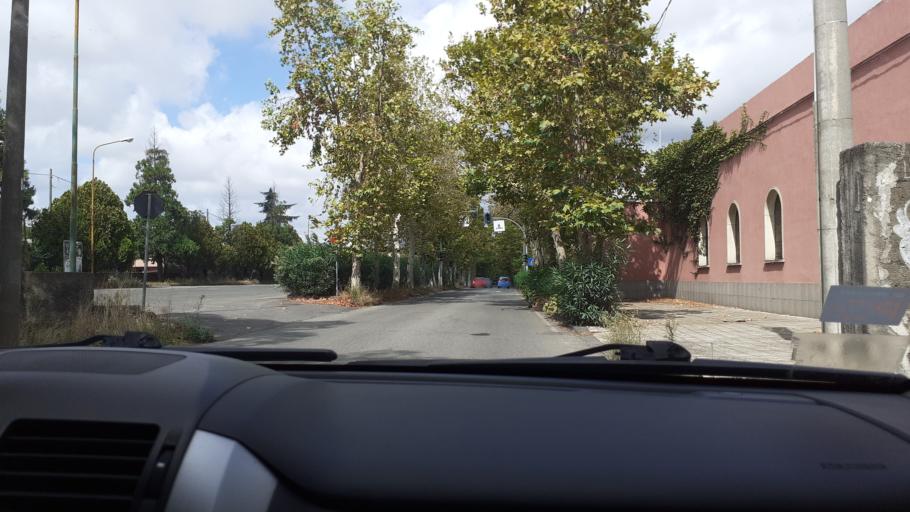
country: IT
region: Sicily
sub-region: Catania
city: San Gregorio di Catania
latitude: 37.5687
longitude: 15.1045
